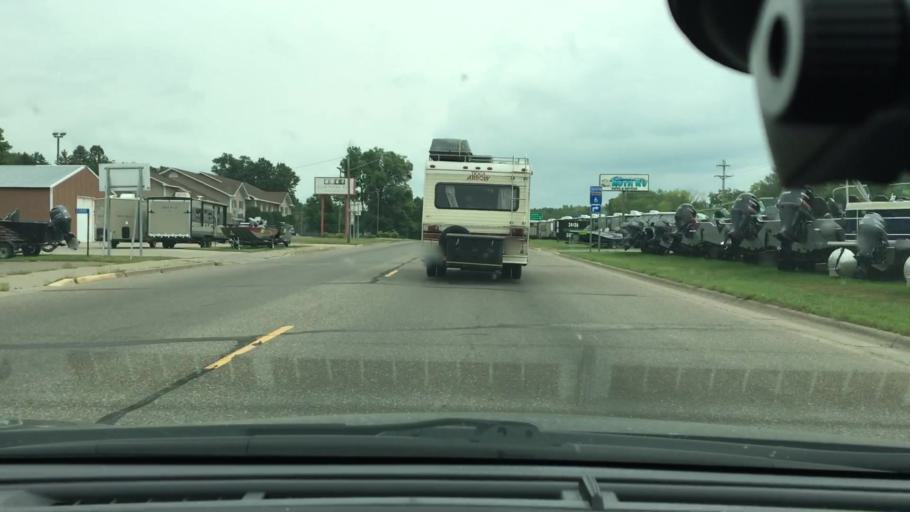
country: US
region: Minnesota
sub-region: Crow Wing County
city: Crosby
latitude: 46.4739
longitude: -93.8987
